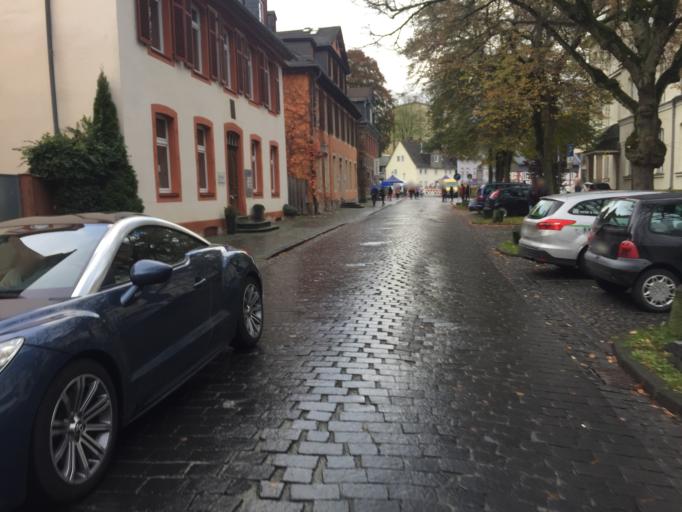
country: DE
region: Hesse
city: Dillenburg
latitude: 50.7365
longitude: 8.2884
